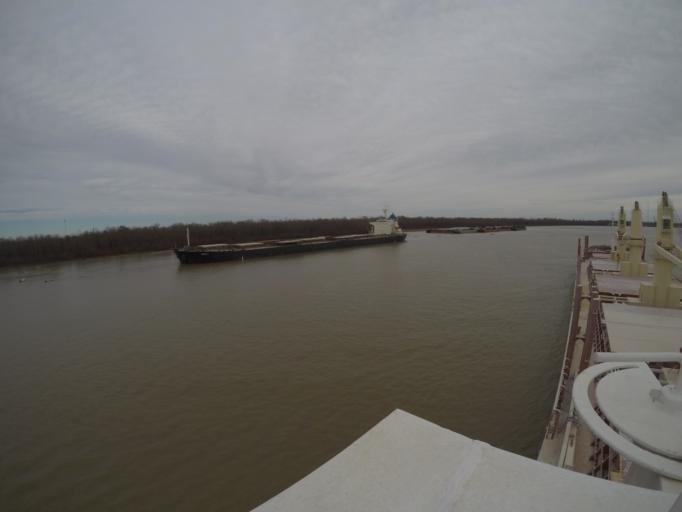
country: US
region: Louisiana
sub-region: Saint John the Baptist Parish
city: Montegut
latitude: 30.0524
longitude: -90.4959
